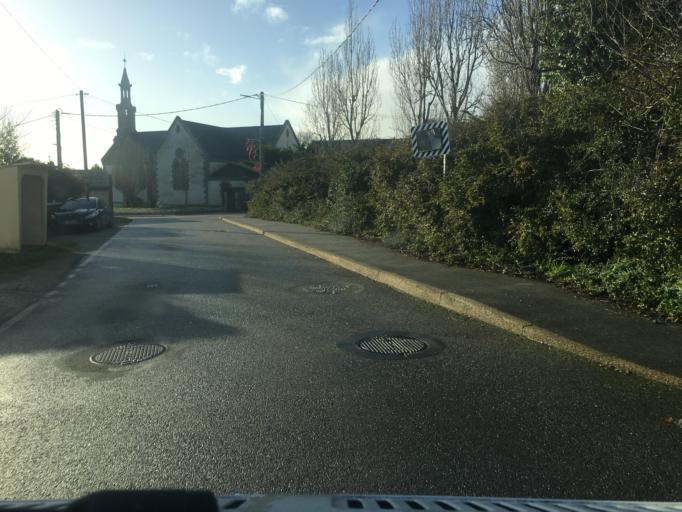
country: FR
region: Brittany
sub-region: Departement du Morbihan
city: Sarzeau
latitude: 47.5074
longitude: -2.6840
